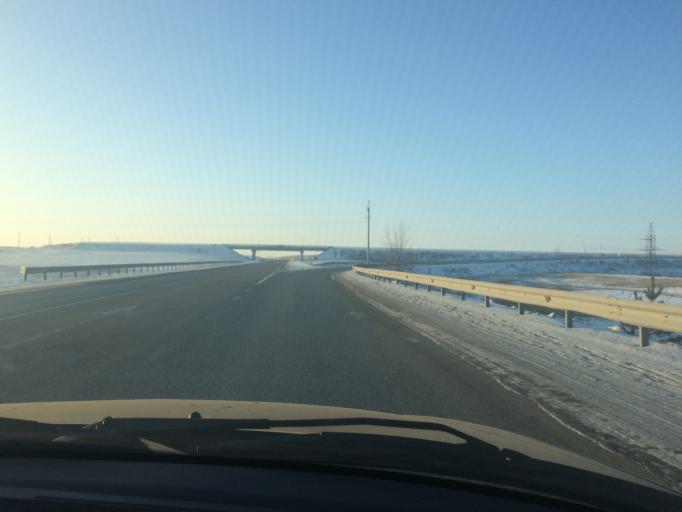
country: RU
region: Chelyabinsk
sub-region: Gorod Magnitogorsk
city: Magnitogorsk
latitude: 53.5839
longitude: 59.1109
